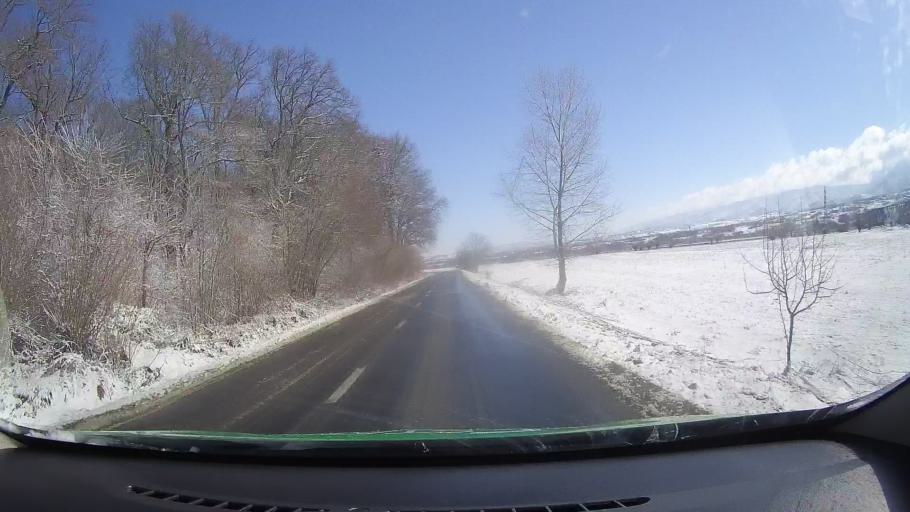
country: RO
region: Sibiu
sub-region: Comuna Turnu Rosu
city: Turnu Rosu
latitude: 45.6627
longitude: 24.3034
